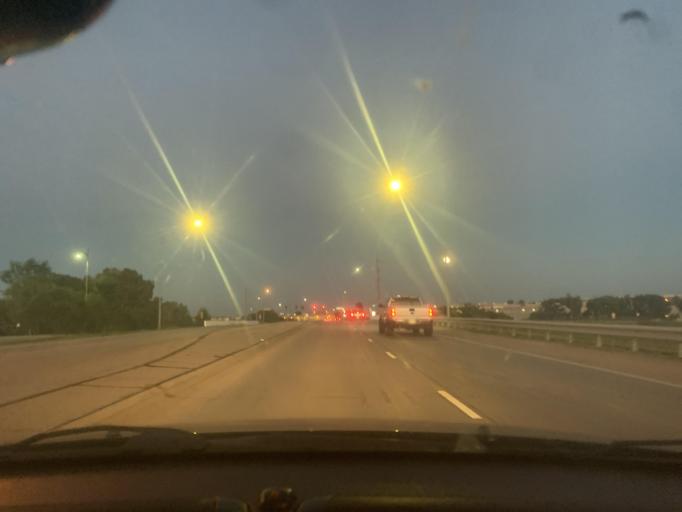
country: US
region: Nebraska
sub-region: Sarpy County
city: Chalco
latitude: 41.1776
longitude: -96.1017
